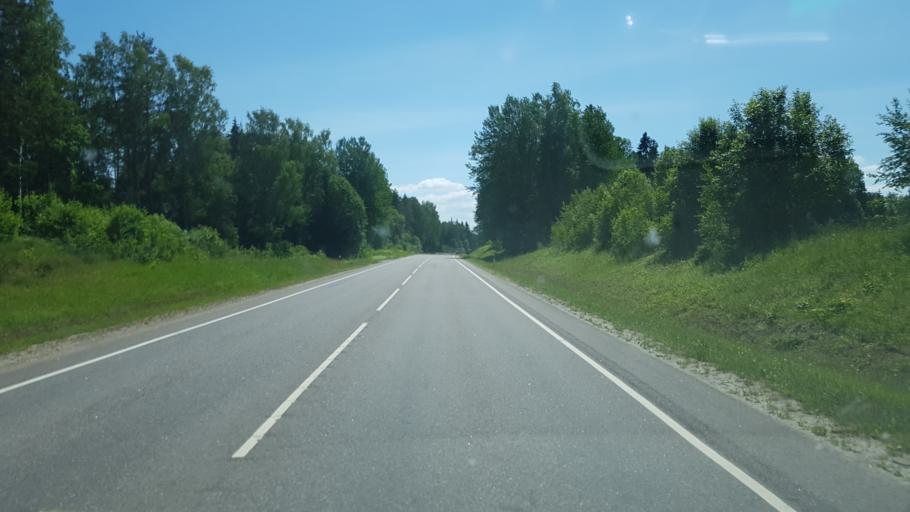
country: EE
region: Tartu
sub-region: UElenurme vald
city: Ulenurme
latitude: 58.1067
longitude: 26.7389
